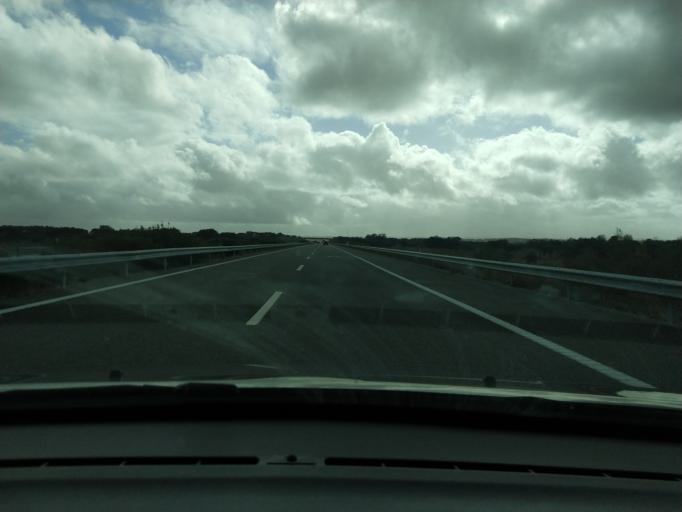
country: PT
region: Beja
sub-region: Ourique
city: Ourique
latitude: 37.5913
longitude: -8.1785
